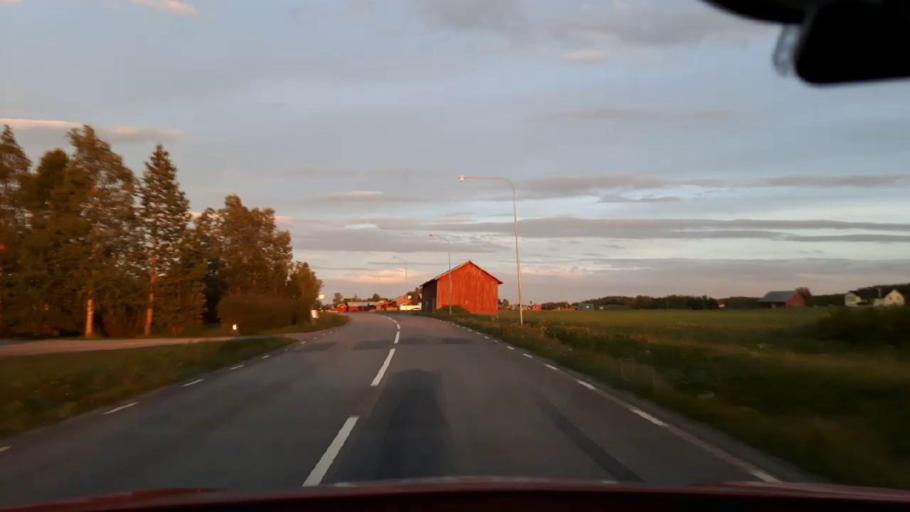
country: SE
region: Jaemtland
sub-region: OEstersunds Kommun
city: Brunflo
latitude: 63.1018
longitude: 14.7386
